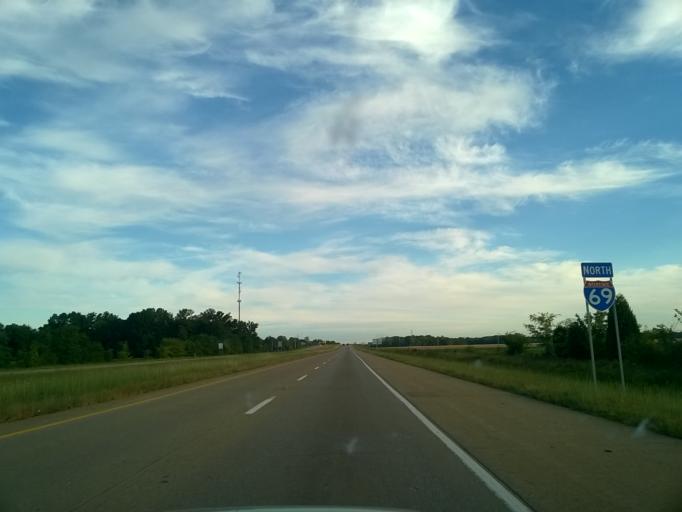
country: US
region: Indiana
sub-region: Vanderburgh County
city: Melody Hill
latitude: 38.0224
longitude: -87.4709
